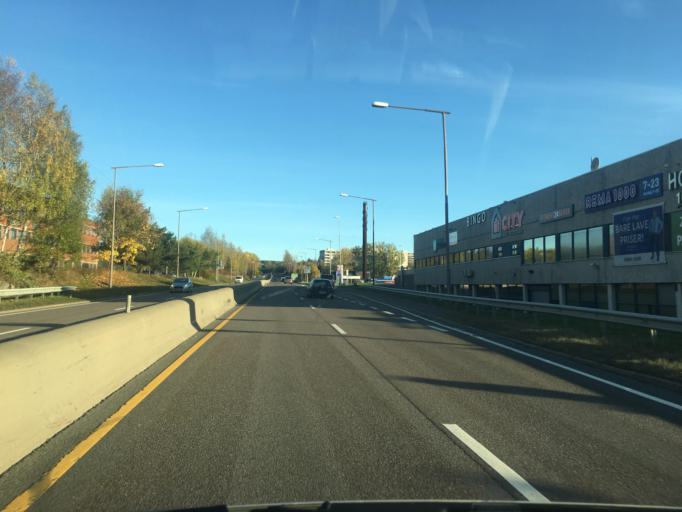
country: NO
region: Akershus
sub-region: Lorenskog
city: Kjenn
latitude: 59.9537
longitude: 10.9075
